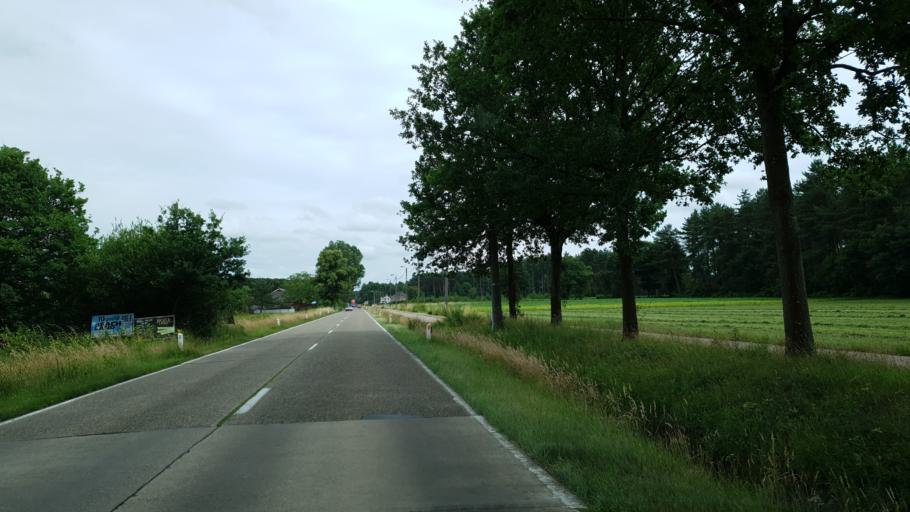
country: BE
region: Flanders
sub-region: Provincie Vlaams-Brabant
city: Scherpenheuvel-Zichem
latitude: 51.0461
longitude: 4.9531
